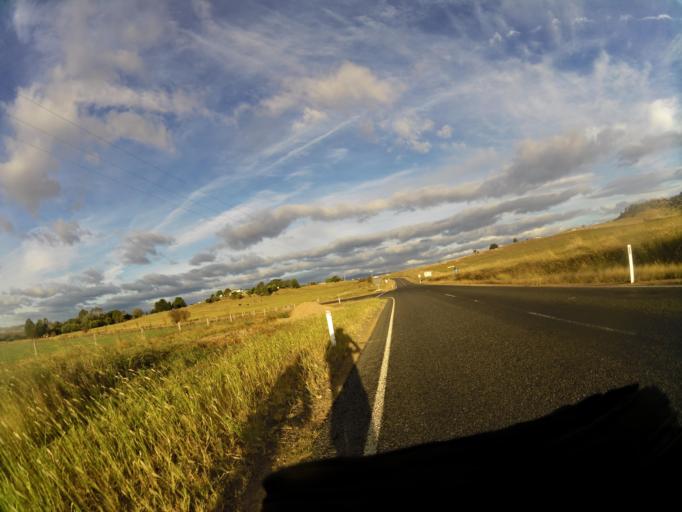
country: AU
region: New South Wales
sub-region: Greater Hume Shire
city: Holbrook
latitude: -36.0490
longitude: 147.9236
